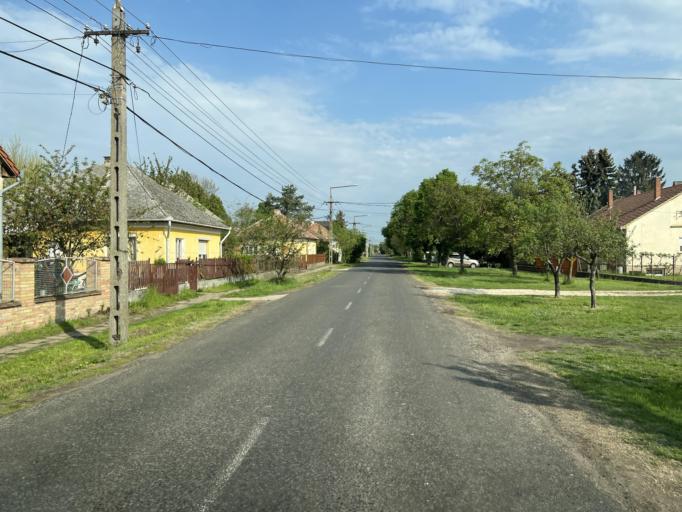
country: HU
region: Pest
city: Abony
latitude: 47.1757
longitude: 20.0151
